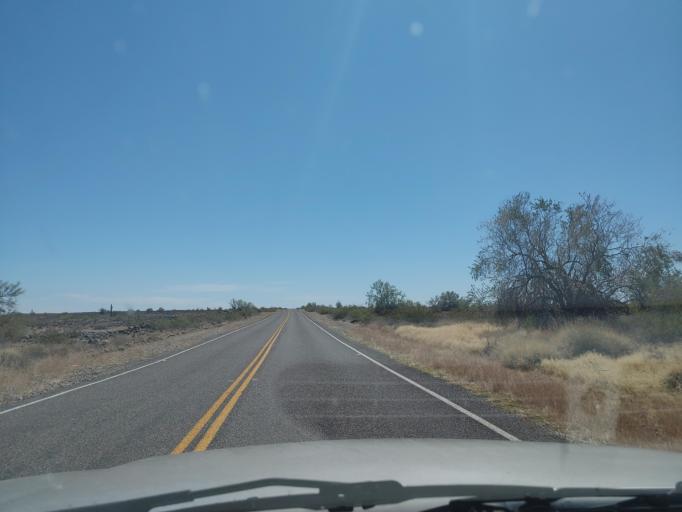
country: US
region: Arizona
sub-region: Maricopa County
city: Gila Bend
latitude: 32.9061
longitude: -113.2645
